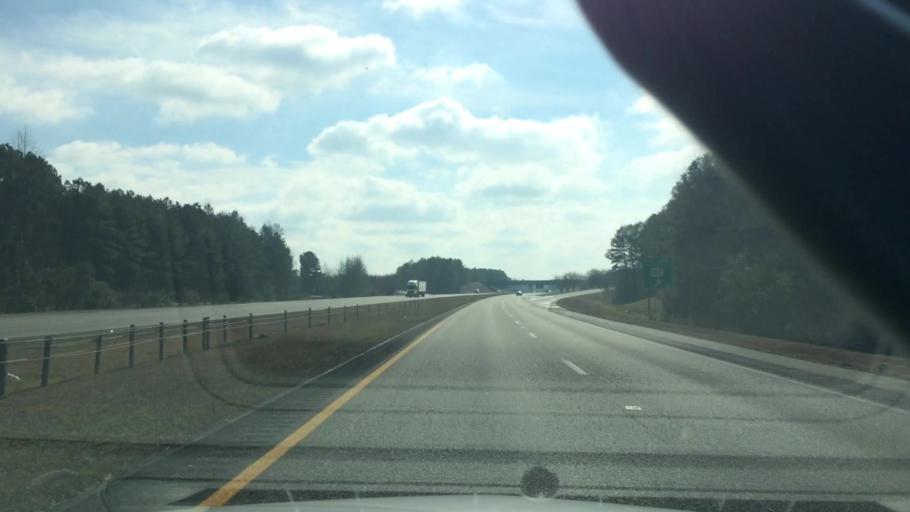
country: US
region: North Carolina
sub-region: Duplin County
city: Wallace
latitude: 34.6923
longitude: -77.9453
